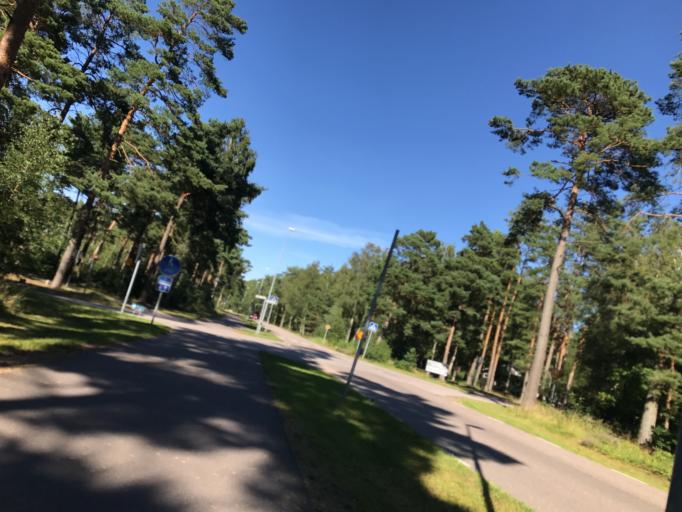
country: SE
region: Skane
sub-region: Bastads Kommun
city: Bastad
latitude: 56.4424
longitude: 12.8978
